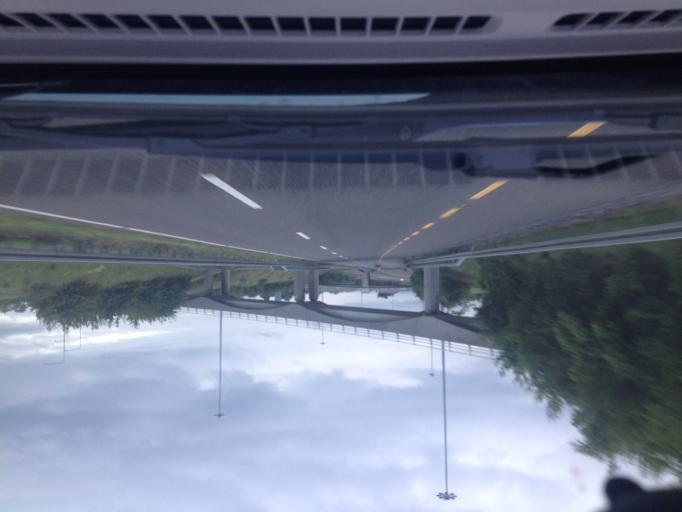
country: IE
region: Connaught
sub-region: Sligo
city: Sligo
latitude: 54.2431
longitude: -8.4798
